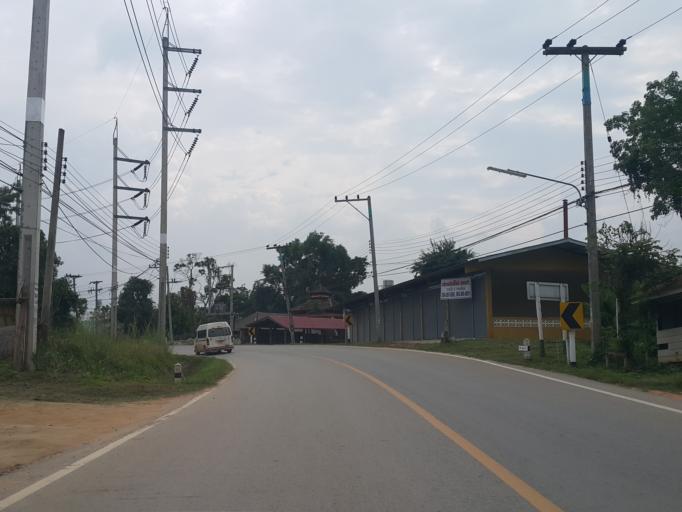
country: TH
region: Chiang Mai
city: Mae Taeng
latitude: 19.1053
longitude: 98.8374
